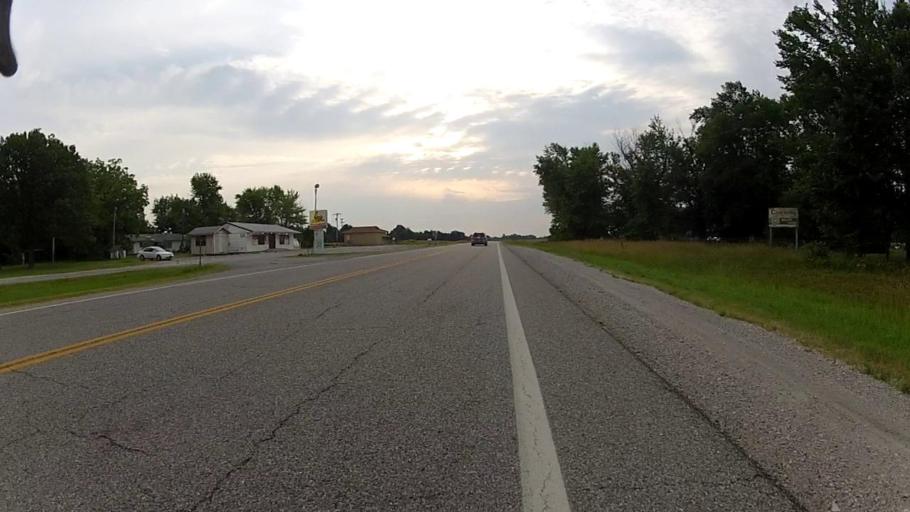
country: US
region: Kansas
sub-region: Labette County
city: Oswego
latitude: 37.1772
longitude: -94.9966
